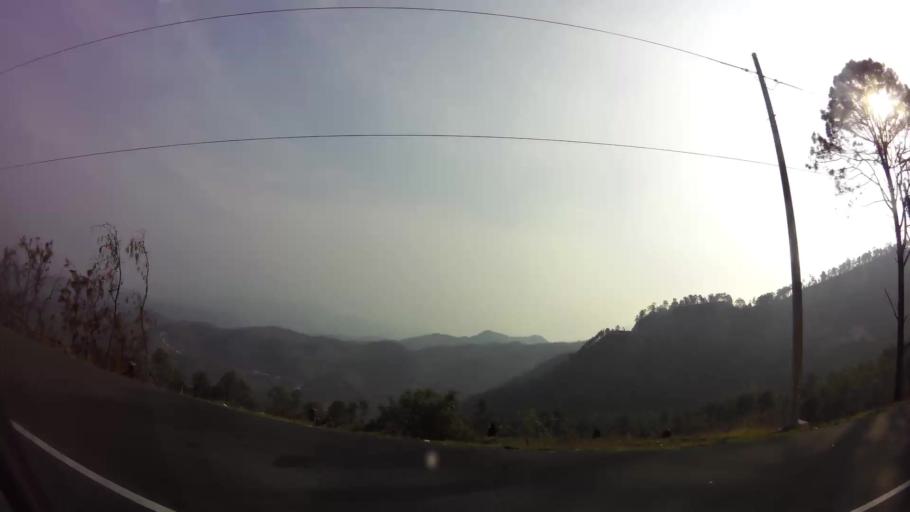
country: HN
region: Comayagua
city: Flores
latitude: 14.2852
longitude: -87.4963
